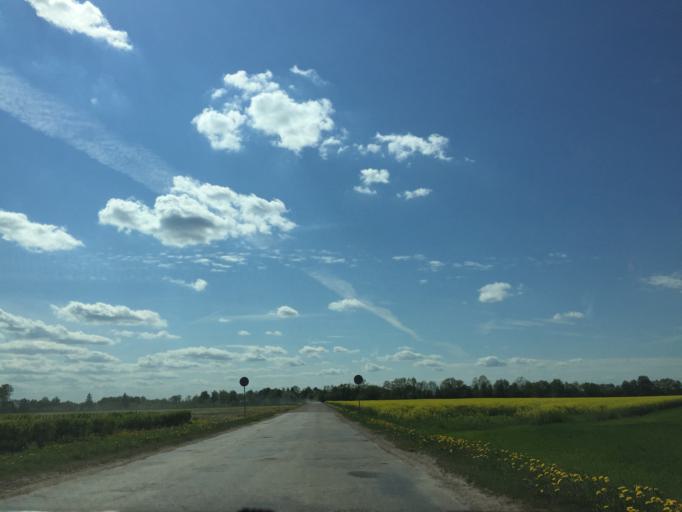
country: LV
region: Rundales
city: Pilsrundale
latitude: 56.4146
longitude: 24.0201
